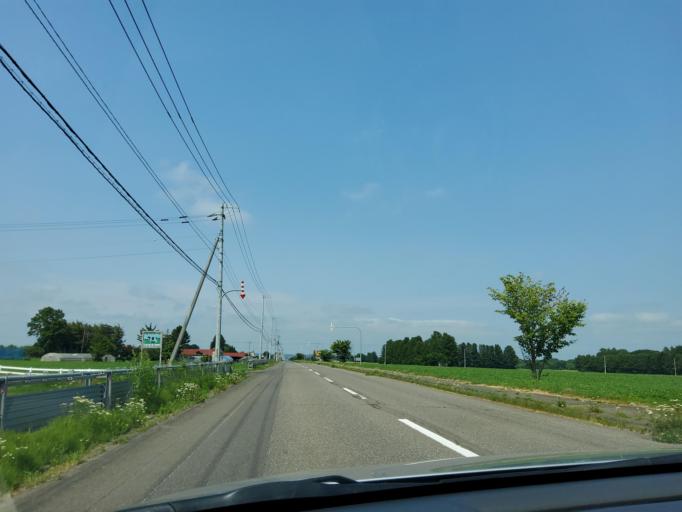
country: JP
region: Hokkaido
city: Obihiro
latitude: 42.8749
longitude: 143.0273
